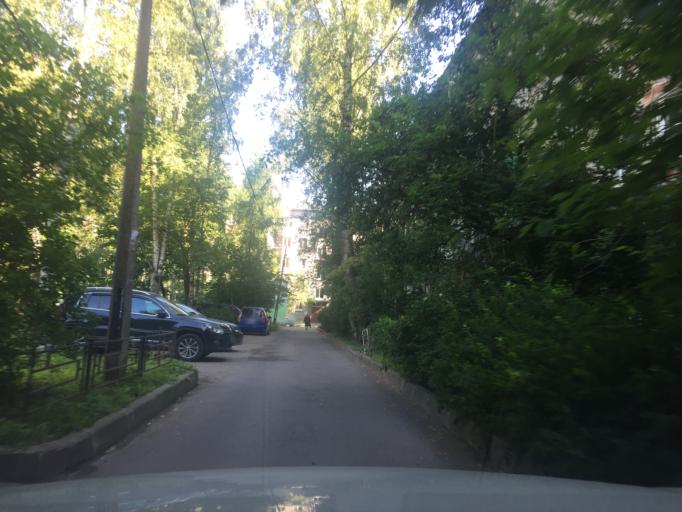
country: RU
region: St.-Petersburg
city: Pushkin
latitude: 59.7349
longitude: 30.4141
